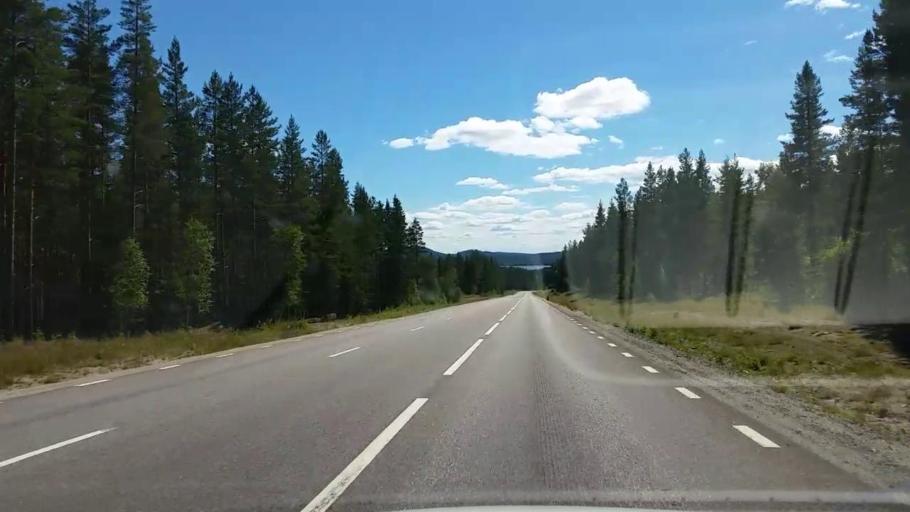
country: SE
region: Gaevleborg
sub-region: Bollnas Kommun
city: Vittsjo
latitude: 61.0561
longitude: 15.8027
